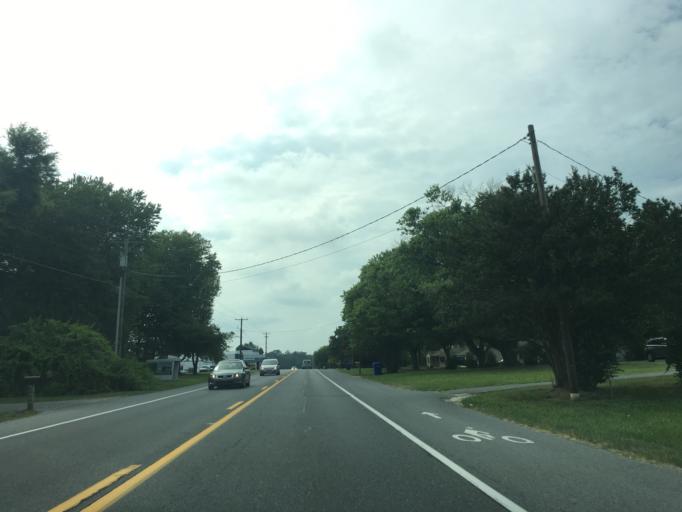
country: US
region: Delaware
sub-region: Sussex County
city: Long Neck
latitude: 38.5550
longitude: -75.1961
